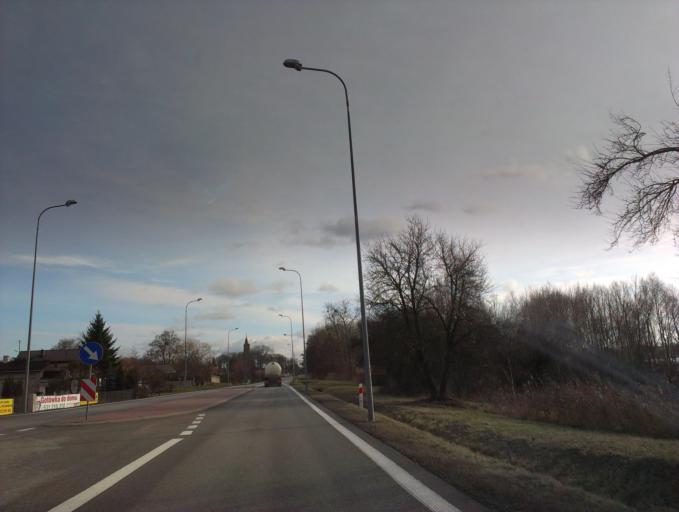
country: PL
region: Kujawsko-Pomorskie
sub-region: Powiat lipnowski
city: Kikol
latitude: 52.9134
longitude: 19.1136
